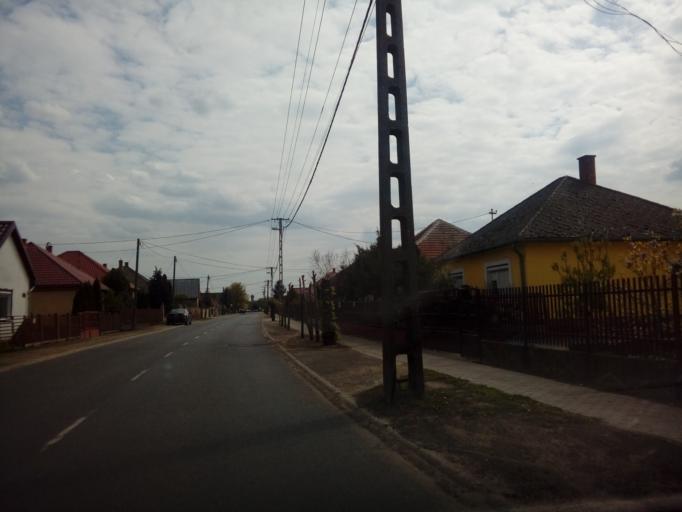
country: HU
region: Szabolcs-Szatmar-Bereg
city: Nagykallo
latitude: 47.8673
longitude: 21.8485
